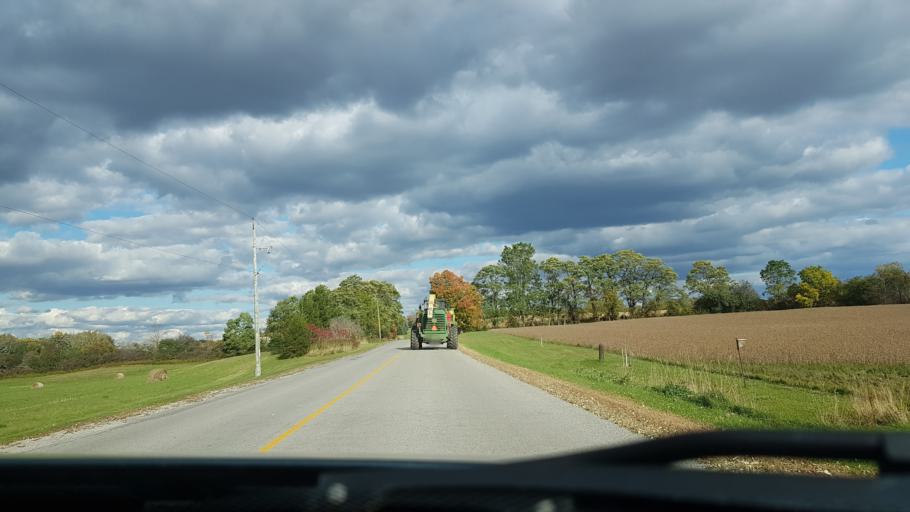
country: CA
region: Ontario
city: Delaware
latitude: 43.0109
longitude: -81.3823
